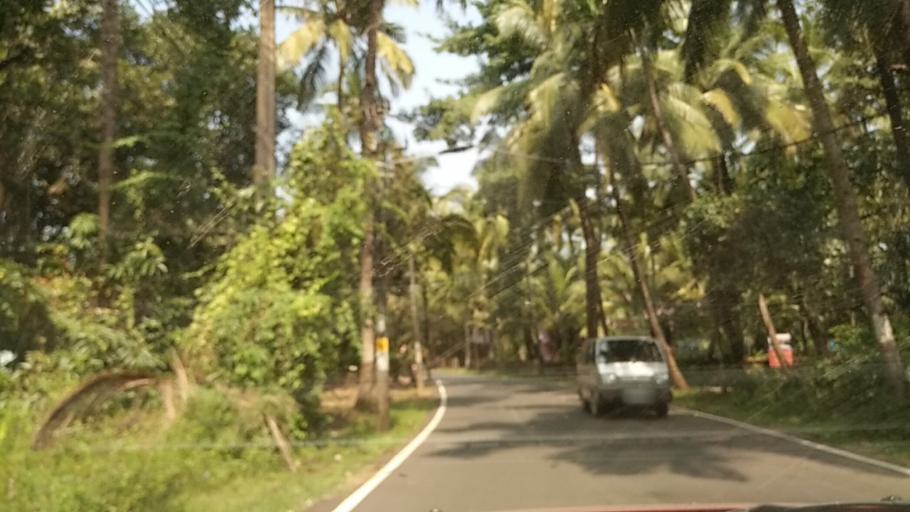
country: IN
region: Goa
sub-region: South Goa
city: Colva
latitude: 15.2915
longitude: 73.9208
